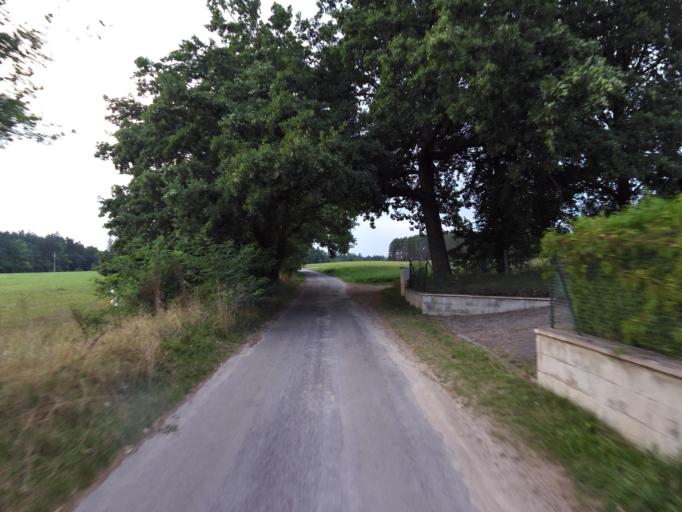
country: CZ
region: Jihocesky
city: Chlum u Trebone
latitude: 48.9810
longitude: 14.9518
